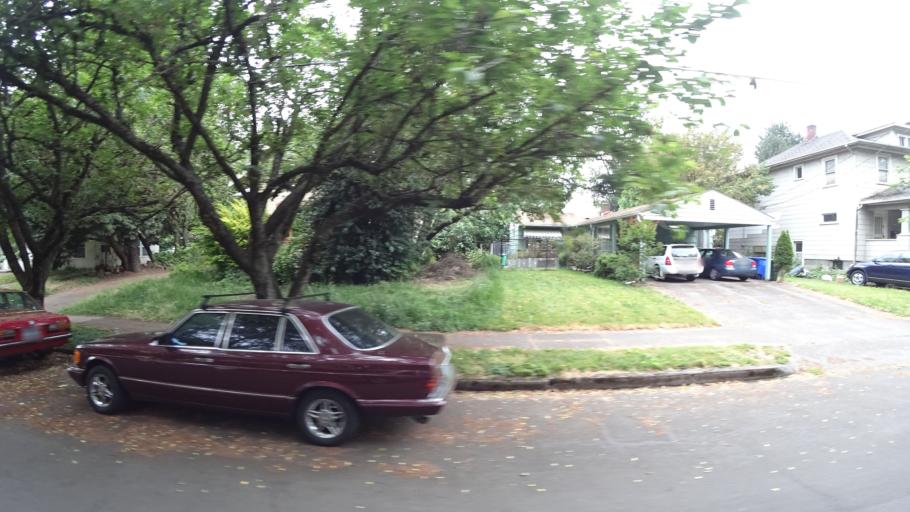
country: US
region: Oregon
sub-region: Multnomah County
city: Portland
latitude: 45.4990
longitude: -122.6578
